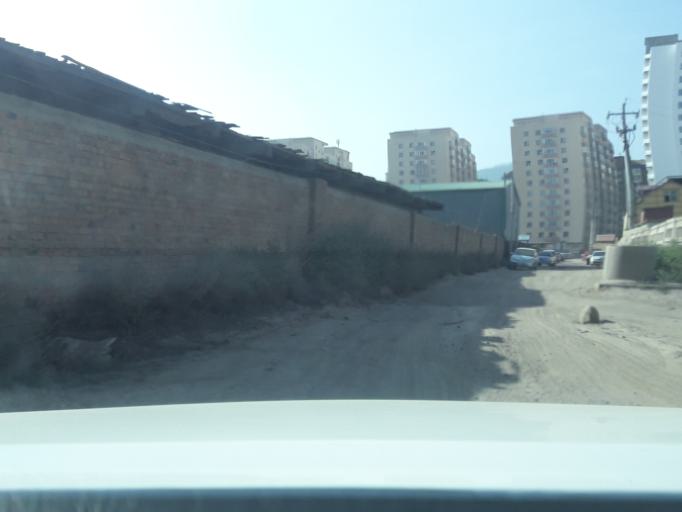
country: MN
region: Ulaanbaatar
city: Ulaanbaatar
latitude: 47.9059
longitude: 106.8835
